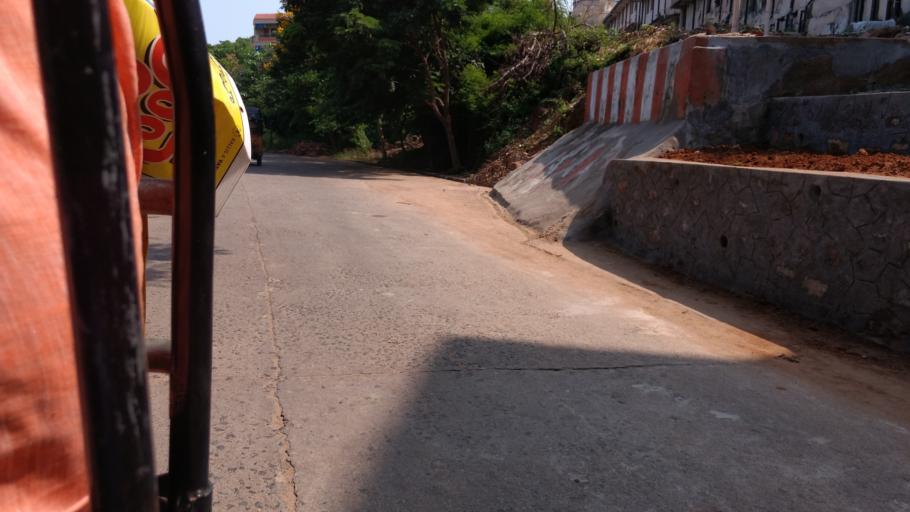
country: IN
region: Andhra Pradesh
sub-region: East Godavari
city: Tuni
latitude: 17.2822
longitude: 82.3994
